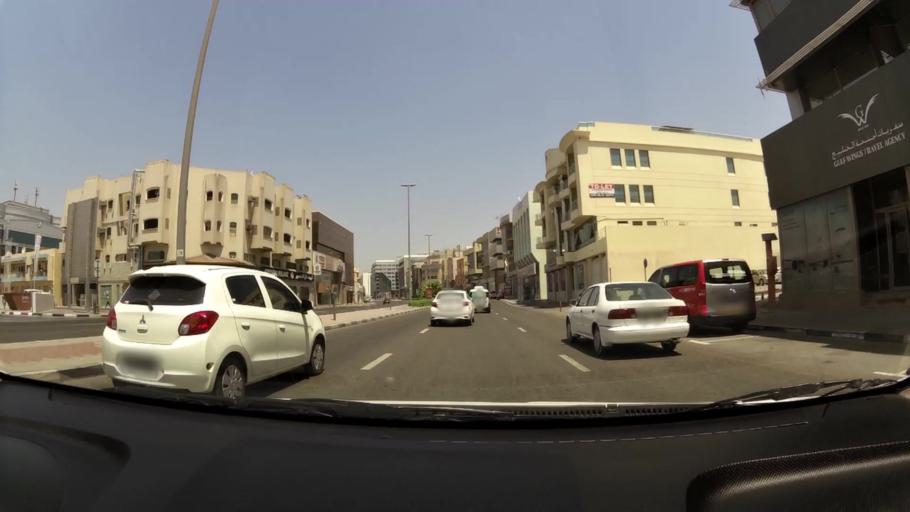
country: AE
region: Ash Shariqah
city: Sharjah
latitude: 25.2623
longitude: 55.3329
